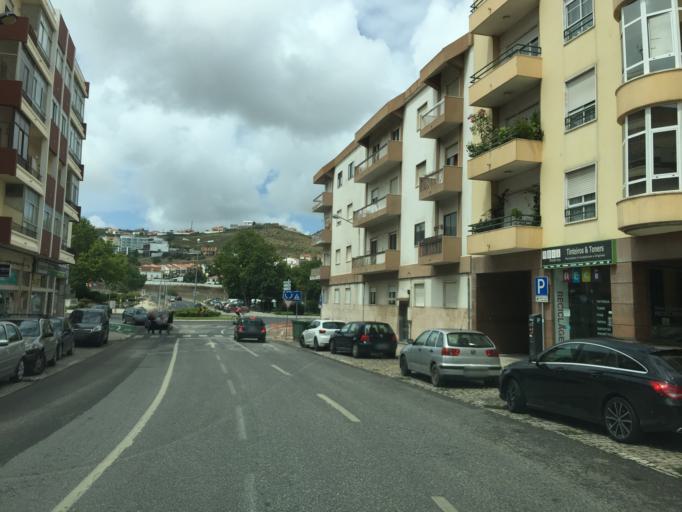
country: PT
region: Lisbon
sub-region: Torres Vedras
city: Torres Vedras
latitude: 39.0882
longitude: -9.2604
